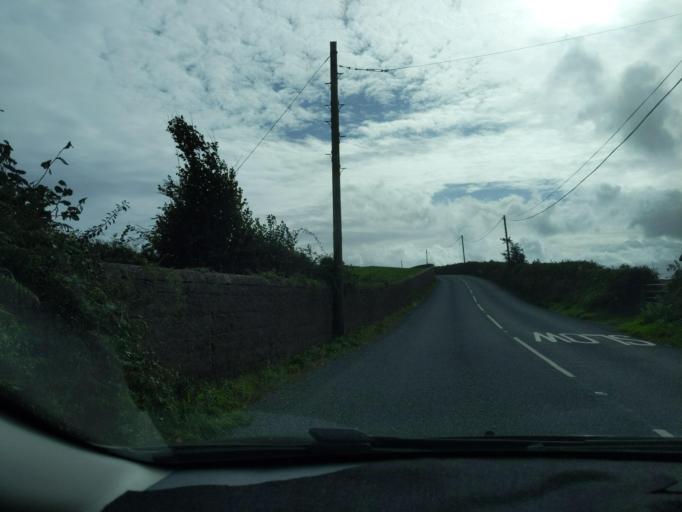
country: GB
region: England
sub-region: Cornwall
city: Mevagissey
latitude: 50.2726
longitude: -4.8288
